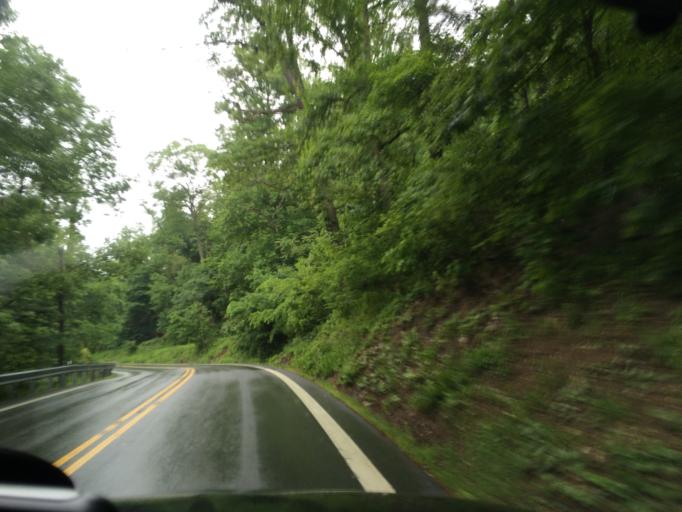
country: US
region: Maryland
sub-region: Frederick County
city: Thurmont
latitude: 39.6495
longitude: -77.4315
